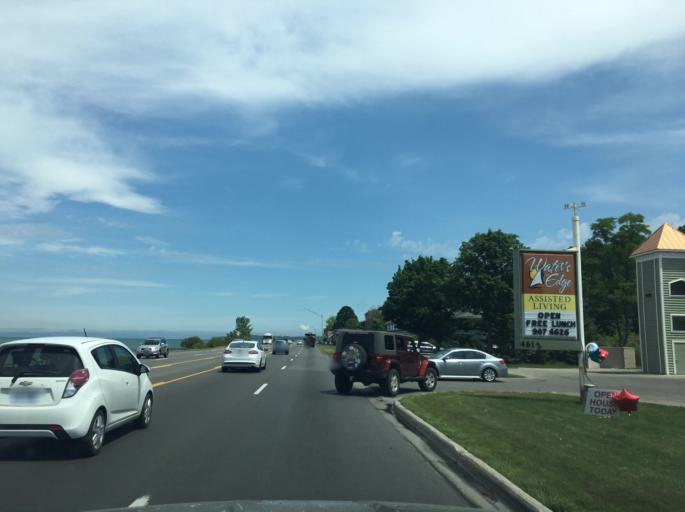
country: US
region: Michigan
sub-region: Grand Traverse County
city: Traverse City
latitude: 44.7500
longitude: -85.5238
